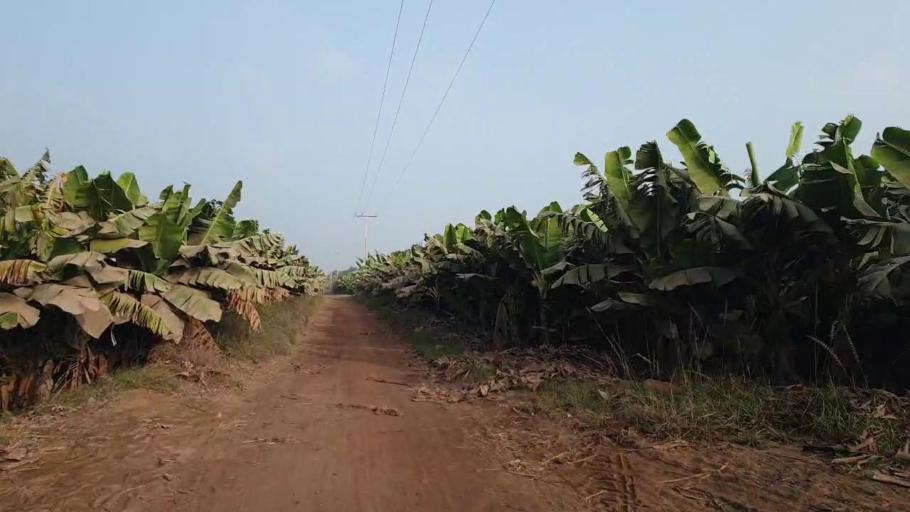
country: PK
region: Sindh
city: Tando Muhammad Khan
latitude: 25.1577
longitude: 68.5853
